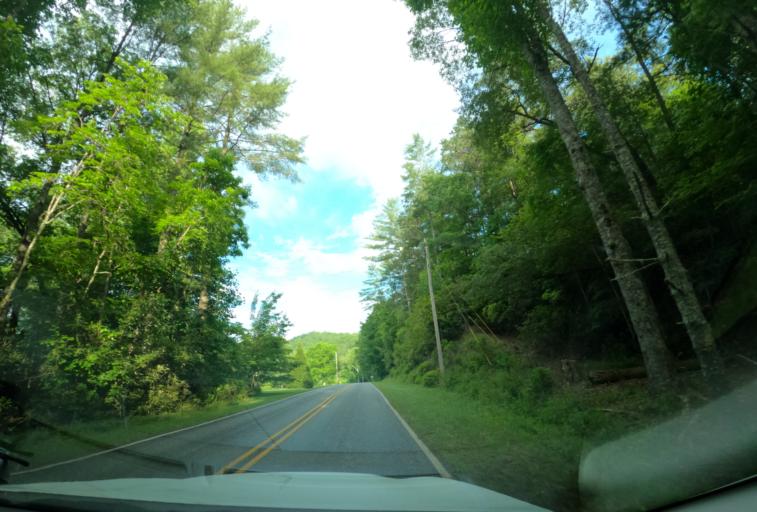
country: US
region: North Carolina
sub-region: Transylvania County
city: Brevard
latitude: 35.1987
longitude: -82.8606
